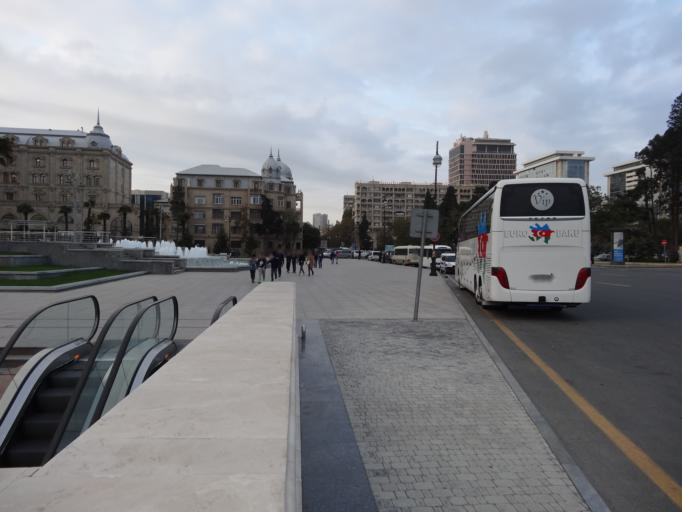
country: AZ
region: Baki
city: Baku
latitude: 40.3720
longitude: 49.8509
